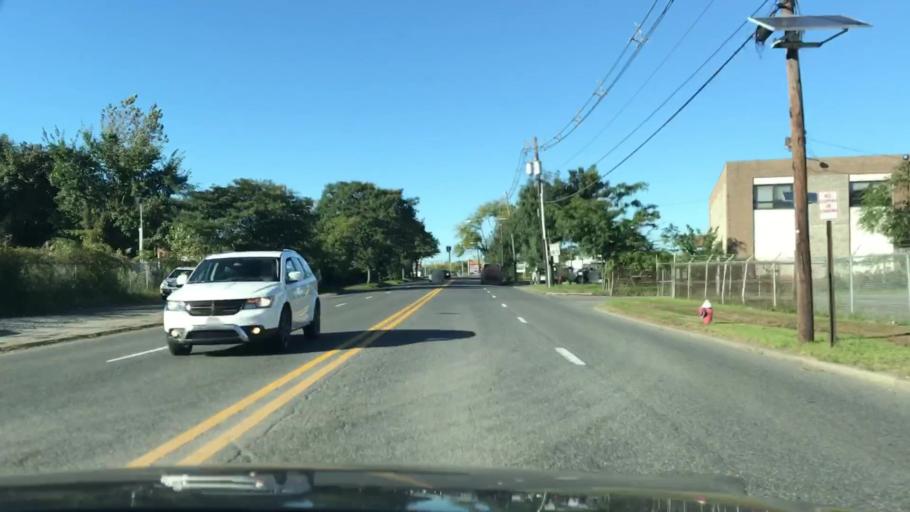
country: US
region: New Jersey
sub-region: Bergen County
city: Little Ferry
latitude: 40.8595
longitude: -74.0352
